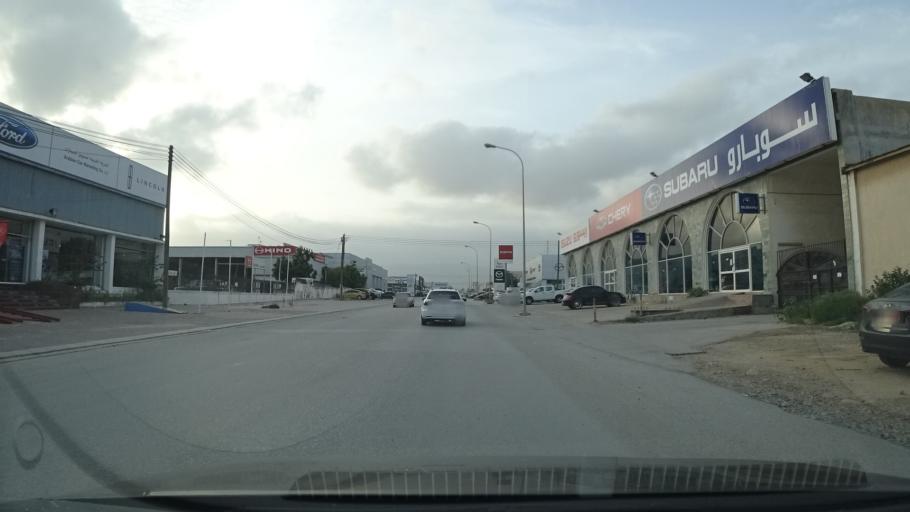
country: OM
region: Zufar
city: Salalah
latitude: 17.0153
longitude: 54.0457
